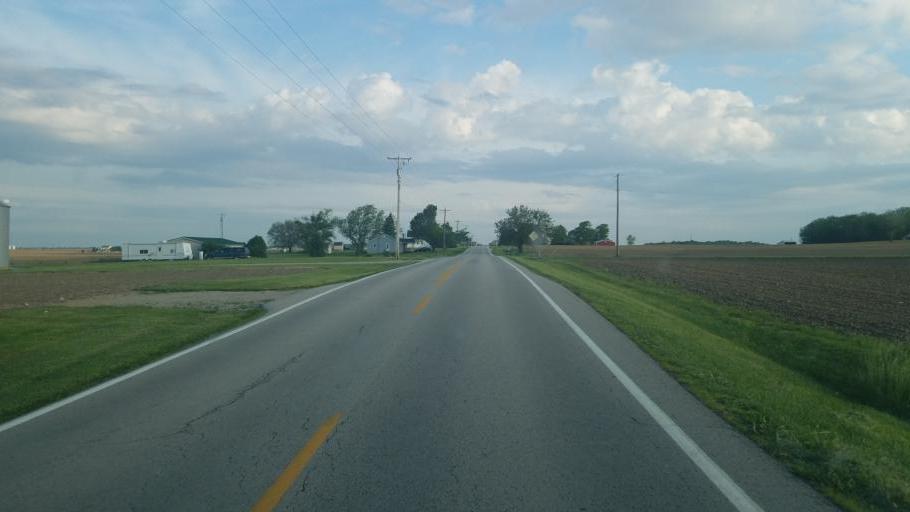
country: US
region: Ohio
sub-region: Clinton County
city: Sabina
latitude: 39.4238
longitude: -83.6223
